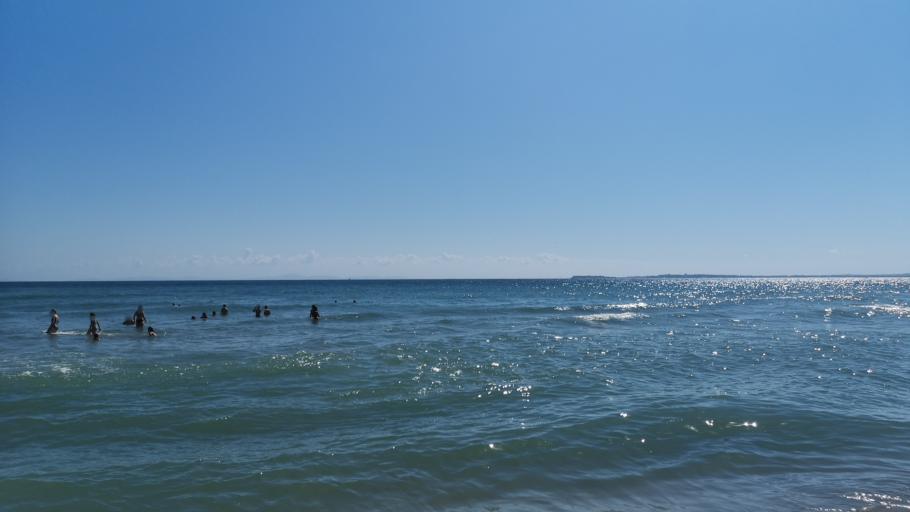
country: BG
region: Burgas
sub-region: Obshtina Nesebur
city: Sveti Vlas
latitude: 42.7027
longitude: 27.8058
